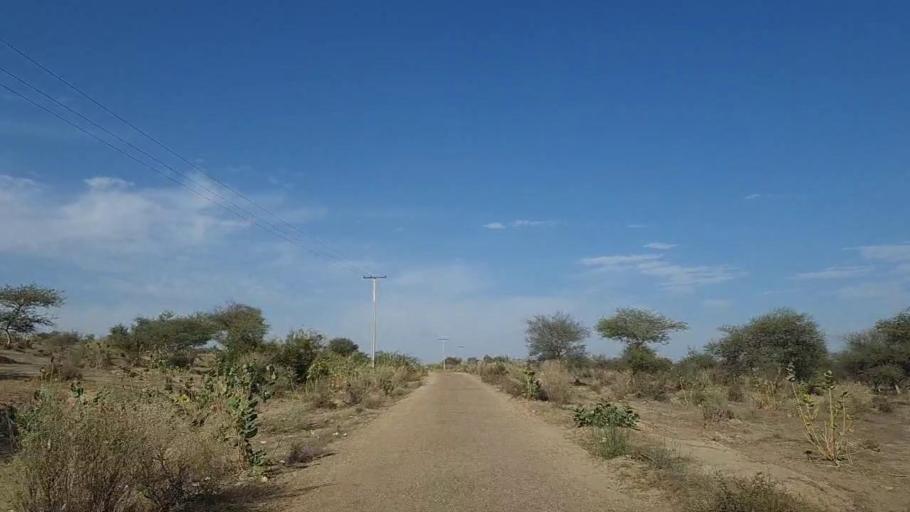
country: PK
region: Sindh
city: Naukot
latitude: 24.8548
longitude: 69.5226
